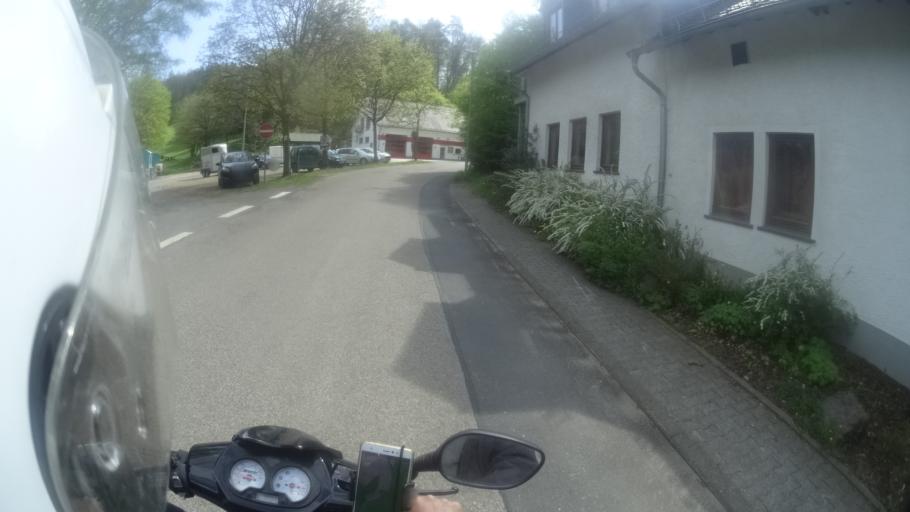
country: DE
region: Hesse
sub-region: Regierungsbezirk Darmstadt
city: Bad Schwalbach
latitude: 50.1035
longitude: 8.0303
